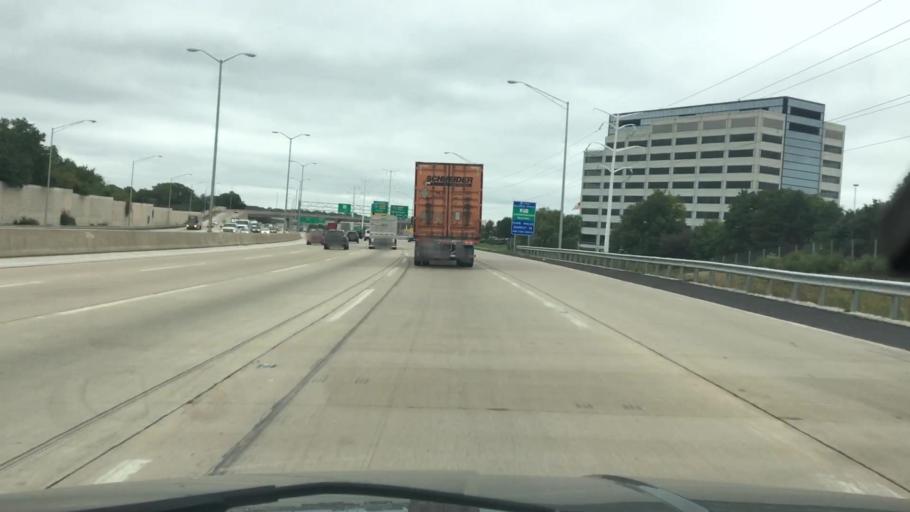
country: US
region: Illinois
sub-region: DuPage County
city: Downers Grove
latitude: 41.8282
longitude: -88.0213
